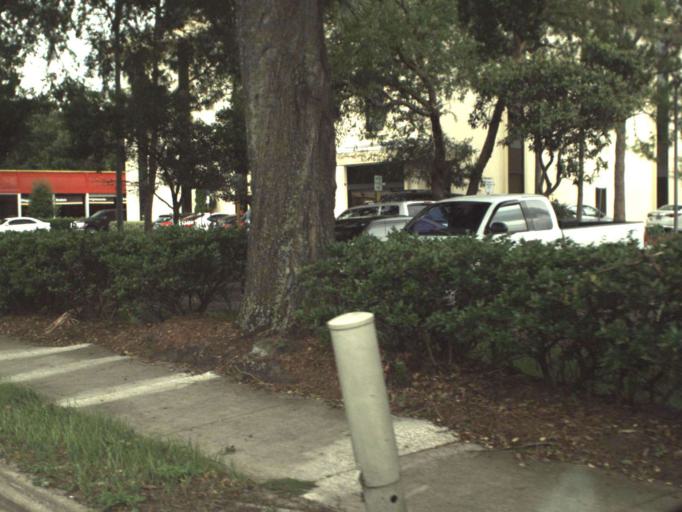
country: US
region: Florida
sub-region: Seminole County
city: Altamonte Springs
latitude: 28.6638
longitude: -81.3704
